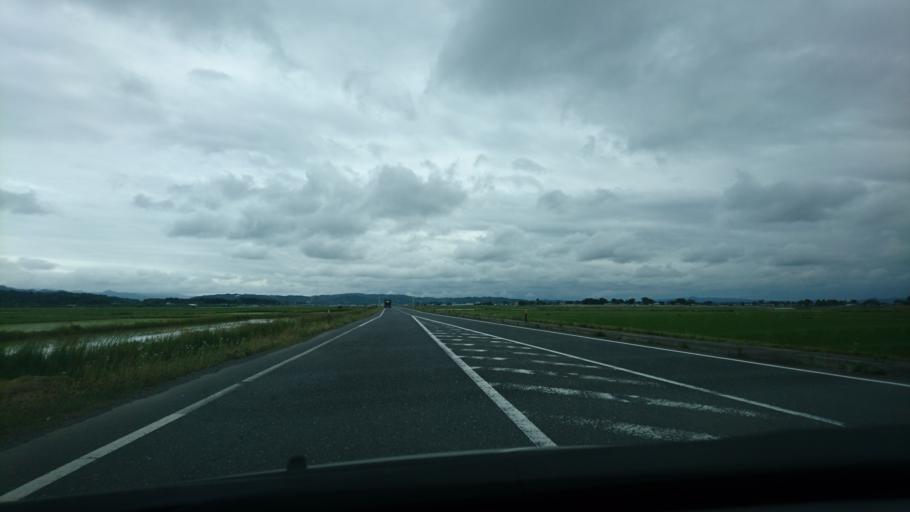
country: JP
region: Miyagi
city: Wakuya
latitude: 38.6892
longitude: 141.2607
